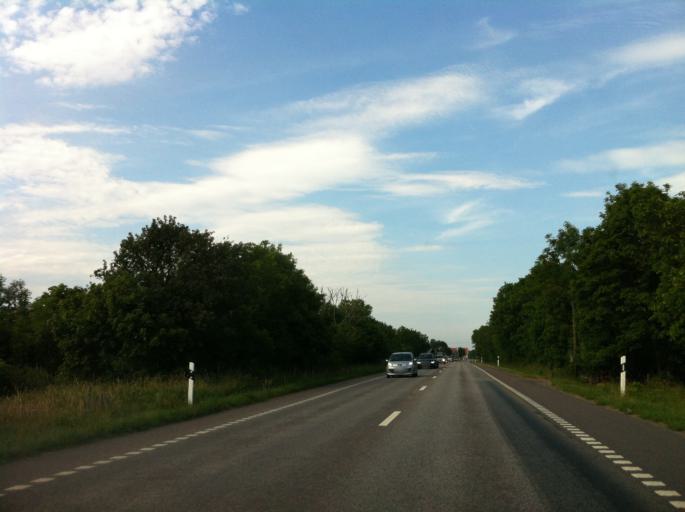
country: SE
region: Kalmar
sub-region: Borgholms Kommun
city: Borgholm
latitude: 56.7942
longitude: 16.5853
